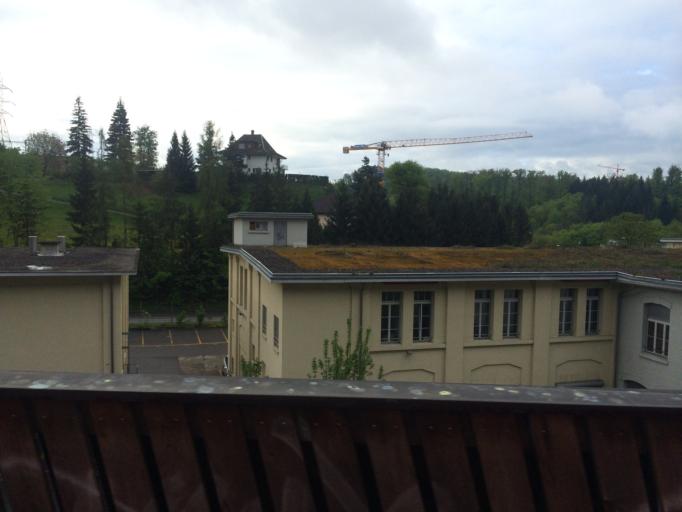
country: CH
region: Bern
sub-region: Bern-Mittelland District
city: Zollikofen
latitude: 46.9787
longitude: 7.4657
